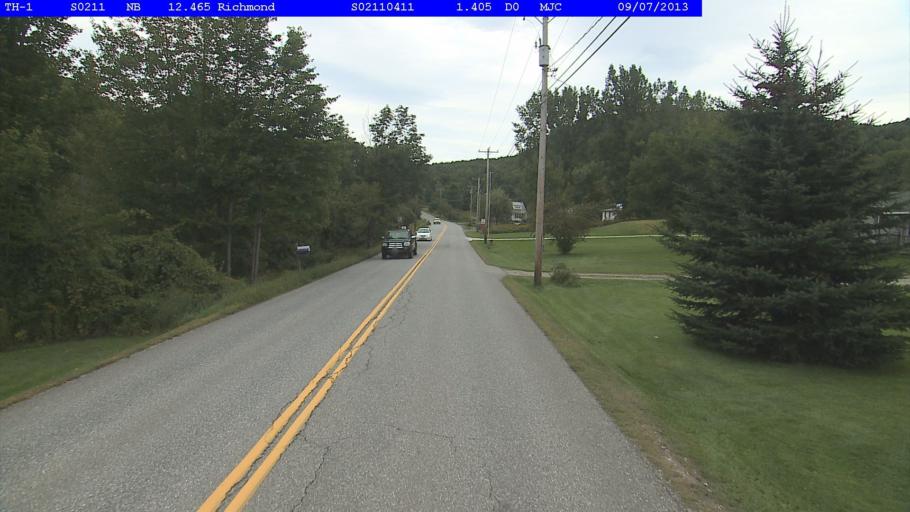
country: US
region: Vermont
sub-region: Chittenden County
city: Williston
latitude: 44.3717
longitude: -72.9999
